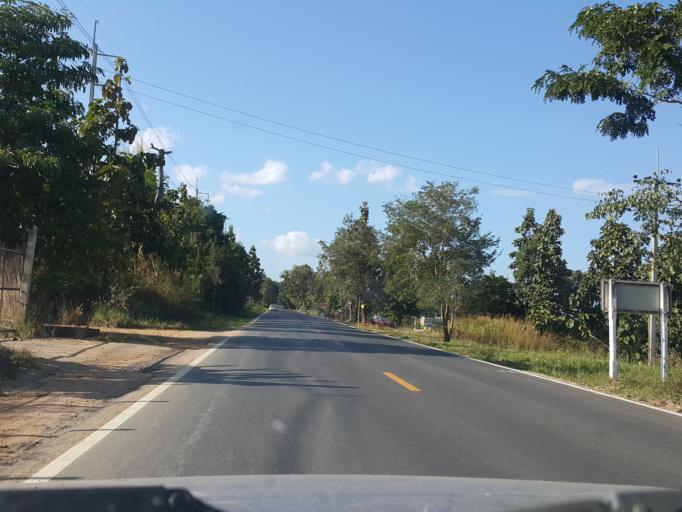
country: TH
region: Mae Hong Son
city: Mae Hi
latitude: 19.3177
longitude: 98.4393
